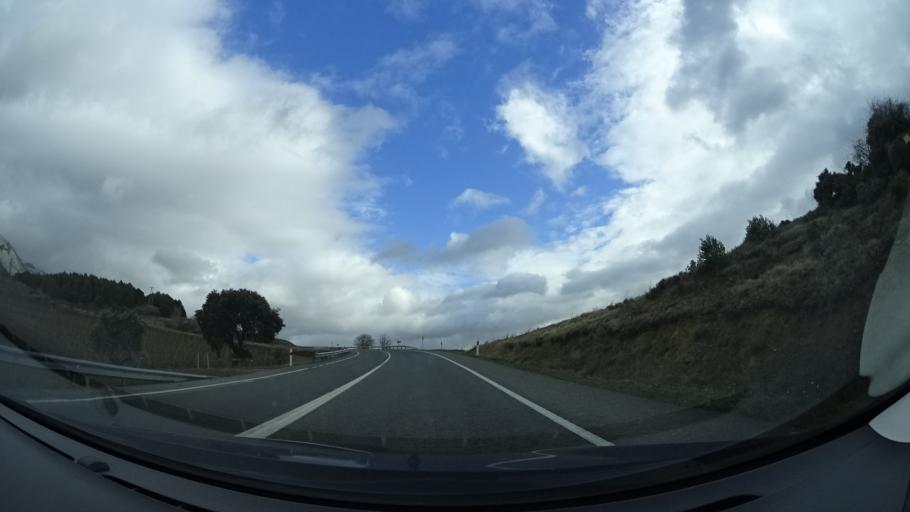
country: ES
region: Basque Country
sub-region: Provincia de Alava
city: Samaniego
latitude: 42.5716
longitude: -2.6604
